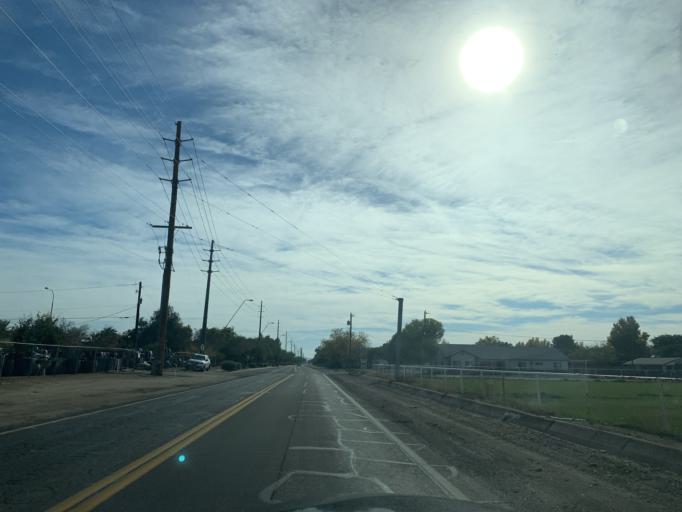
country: US
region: Arizona
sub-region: Maricopa County
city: Sun Lakes
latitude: 33.2305
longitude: -111.8066
